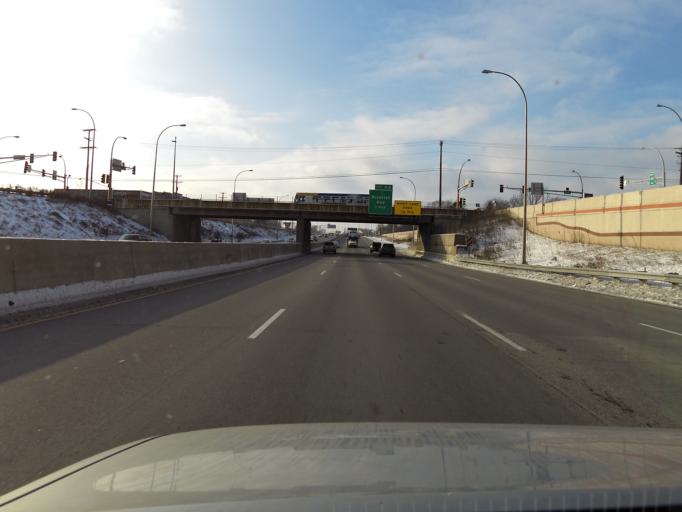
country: US
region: Minnesota
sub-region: Hennepin County
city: Richfield
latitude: 44.8623
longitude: -93.2569
